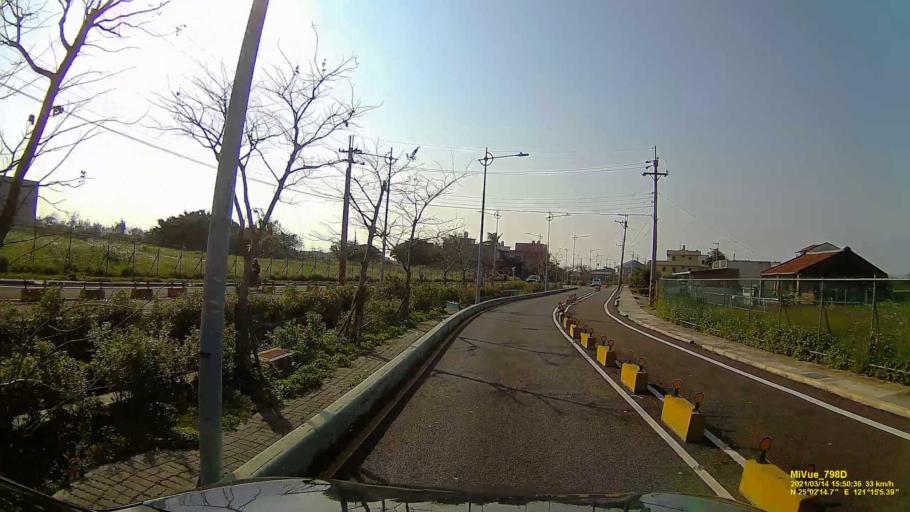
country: TW
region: Taiwan
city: Taoyuan City
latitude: 25.0375
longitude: 121.2515
